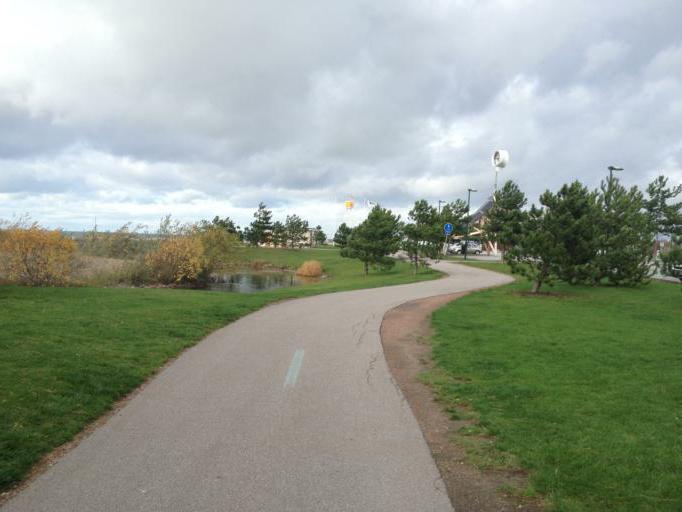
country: SE
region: Skane
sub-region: Malmo
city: Malmoe
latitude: 55.6155
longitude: 12.9749
